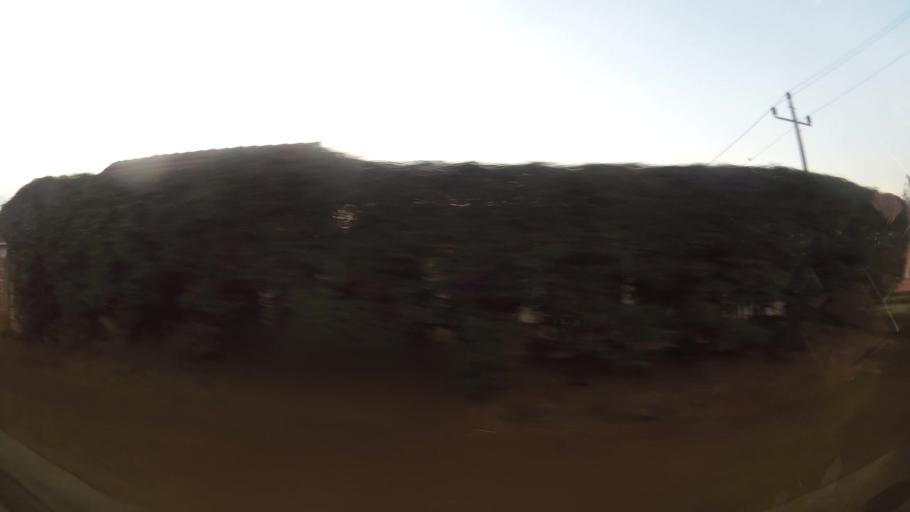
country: ZA
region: Gauteng
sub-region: City of Johannesburg Metropolitan Municipality
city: Orange Farm
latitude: -26.5521
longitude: 27.8773
